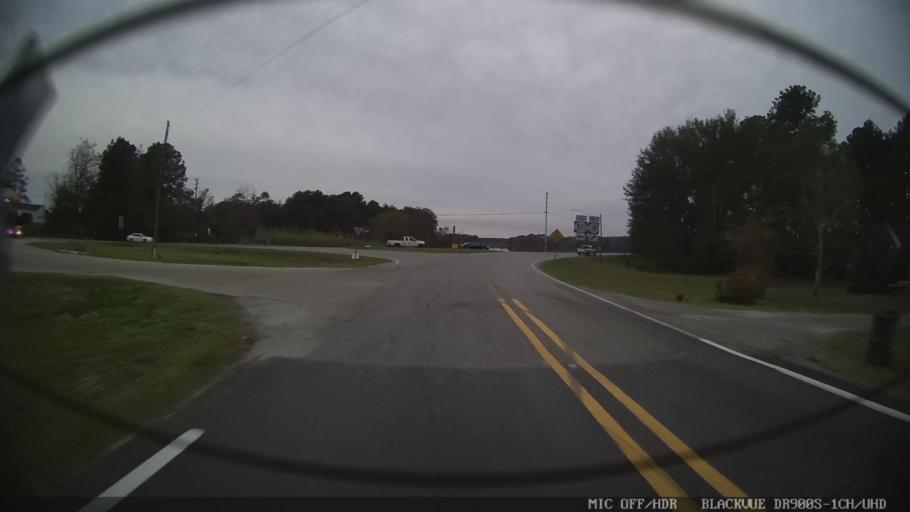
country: US
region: Mississippi
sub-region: Clarke County
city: Quitman
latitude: 32.0401
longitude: -88.7083
